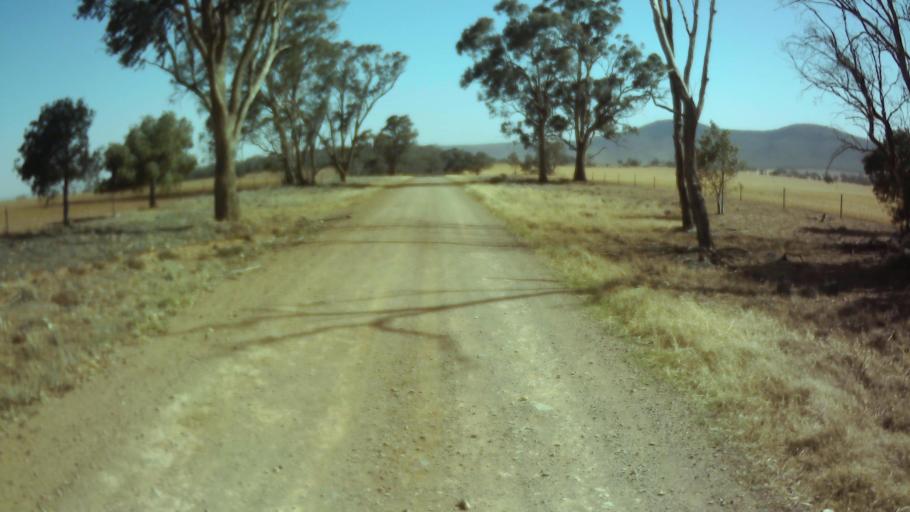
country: AU
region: New South Wales
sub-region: Weddin
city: Grenfell
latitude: -33.8514
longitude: 148.0163
